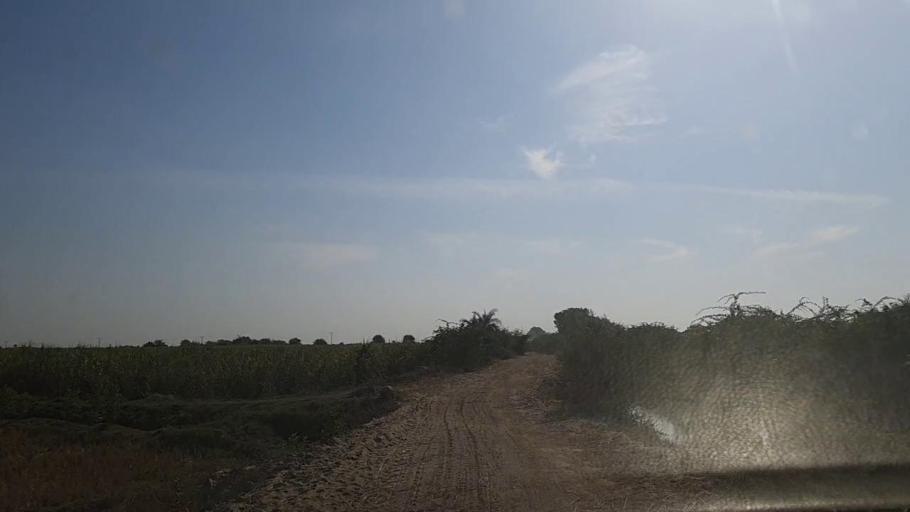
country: PK
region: Sindh
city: Bulri
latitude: 24.8383
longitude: 68.2819
